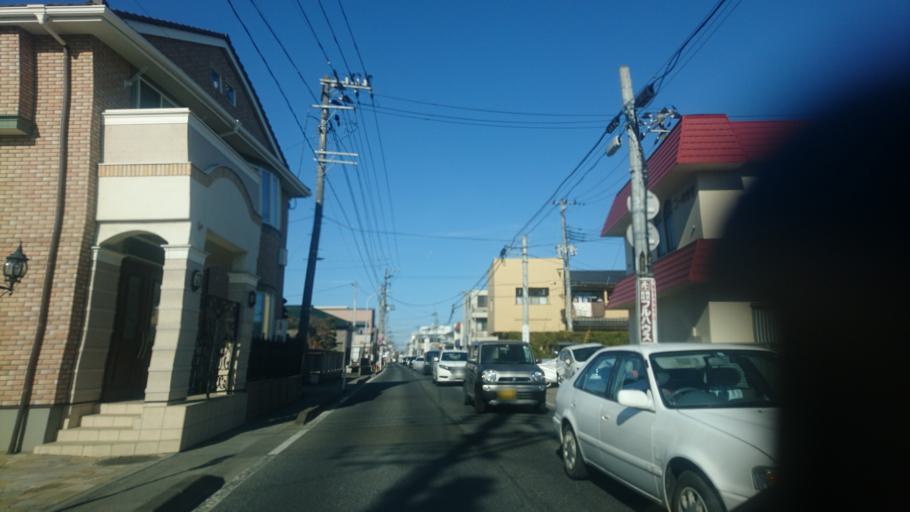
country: JP
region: Miyagi
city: Sendai
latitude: 38.1979
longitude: 140.8851
